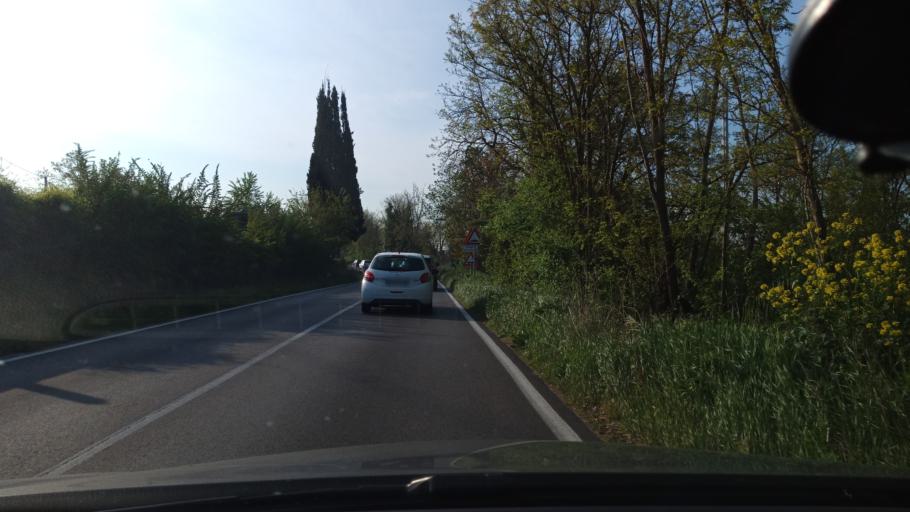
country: IT
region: Latium
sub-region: Citta metropolitana di Roma Capitale
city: Fiano Romano
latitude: 42.1693
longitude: 12.6373
